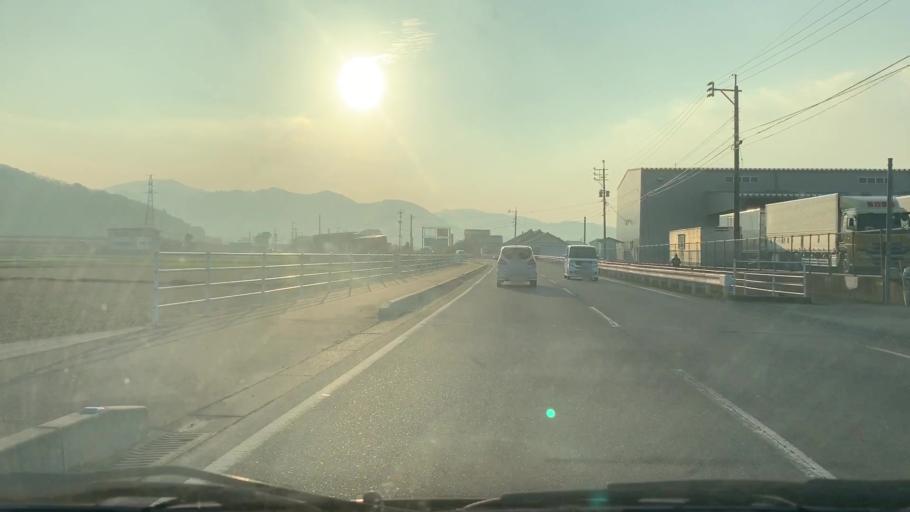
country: JP
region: Saga Prefecture
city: Saga-shi
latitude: 33.2784
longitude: 130.1497
